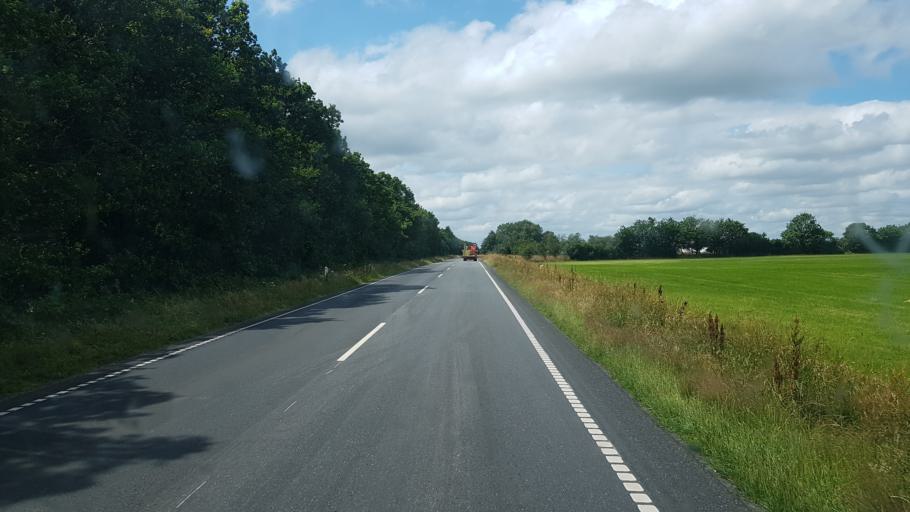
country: DK
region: South Denmark
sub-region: Vejen Kommune
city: Holsted
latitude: 55.5142
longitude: 8.8629
